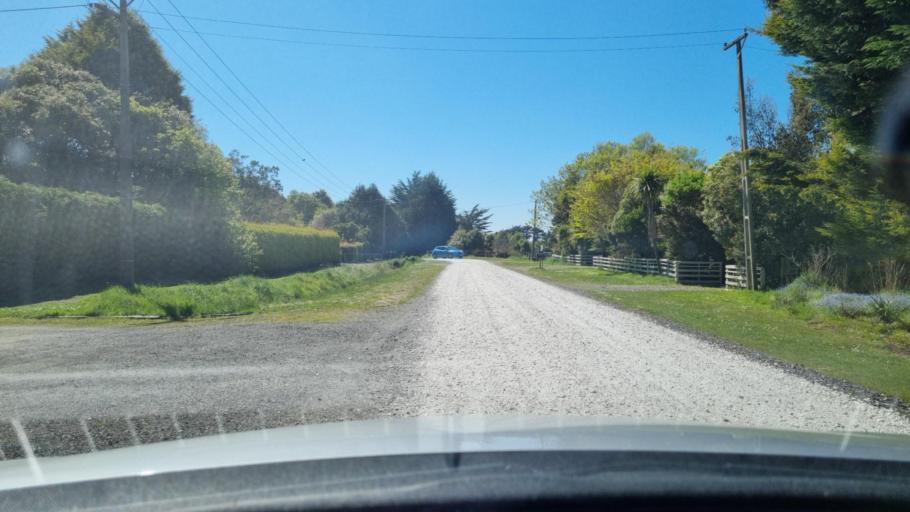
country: NZ
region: Southland
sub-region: Invercargill City
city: Invercargill
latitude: -46.4413
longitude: 168.3191
